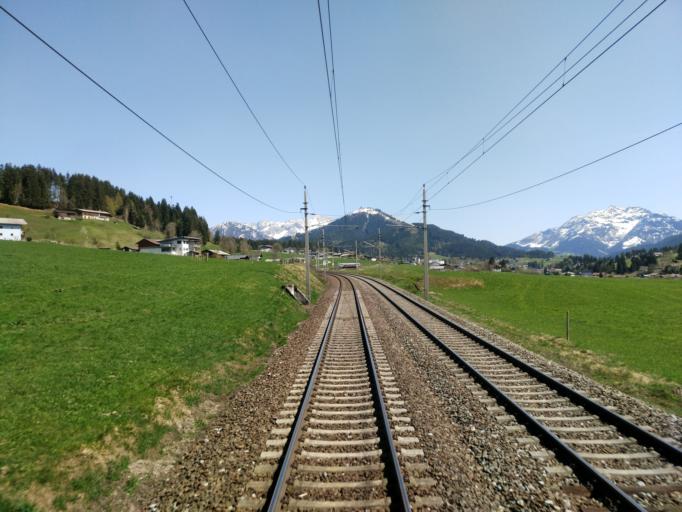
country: AT
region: Tyrol
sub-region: Politischer Bezirk Kitzbuhel
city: Fieberbrunn
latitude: 47.4952
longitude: 12.5097
